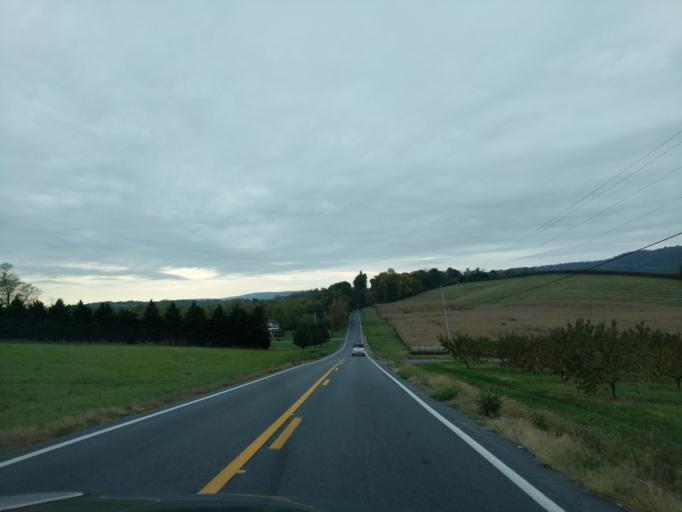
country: US
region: West Virginia
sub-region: Berkeley County
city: Inwood
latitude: 39.4170
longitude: -78.0496
